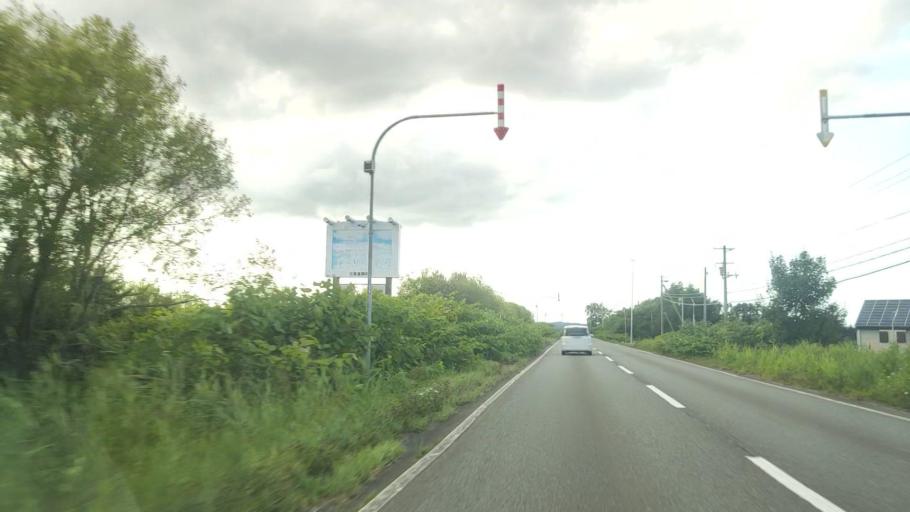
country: JP
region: Hokkaido
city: Makubetsu
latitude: 45.0020
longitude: 141.8156
